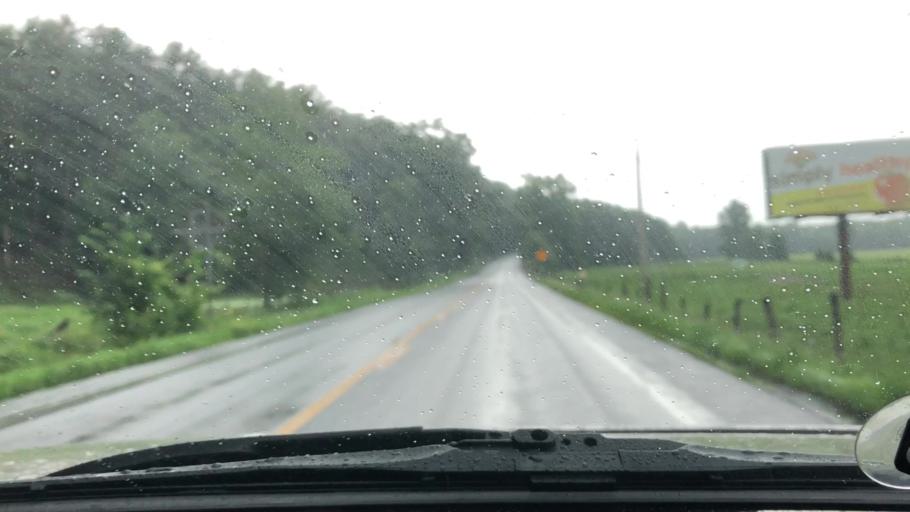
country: US
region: New York
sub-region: Greene County
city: Palenville
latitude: 42.1947
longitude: -73.9859
